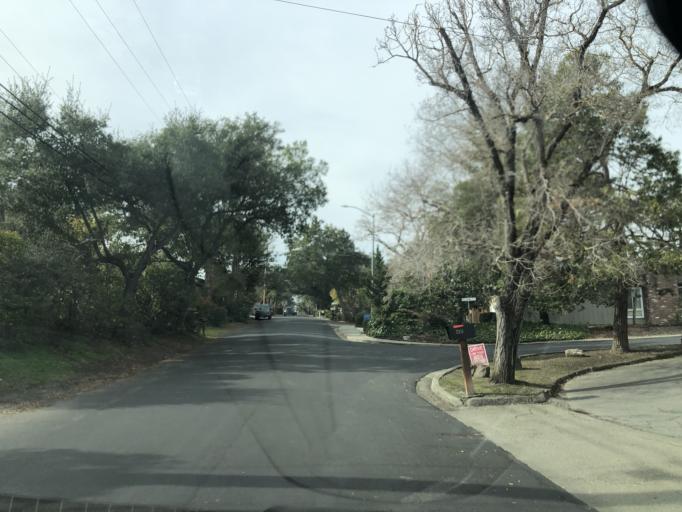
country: US
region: California
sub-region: Contra Costa County
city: Saranap
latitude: 37.8910
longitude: -122.0768
